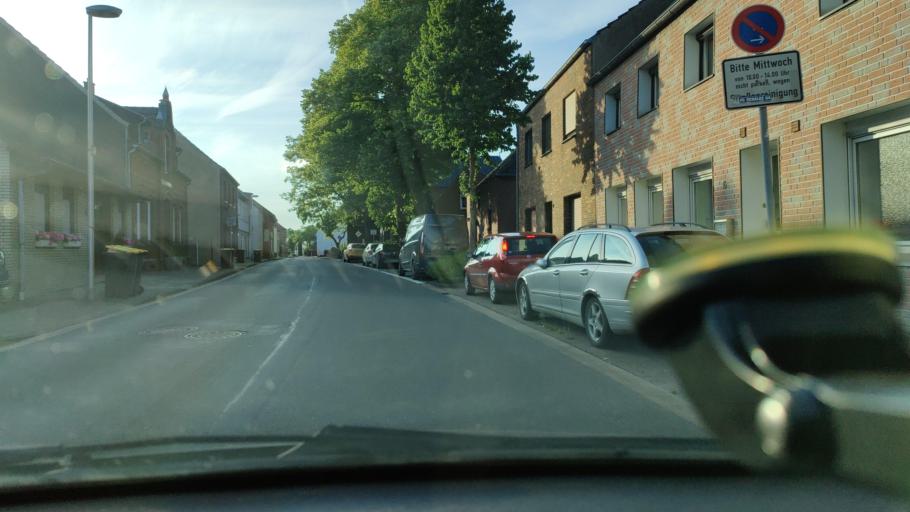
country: DE
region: North Rhine-Westphalia
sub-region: Regierungsbezirk Dusseldorf
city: Rheurdt
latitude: 51.5091
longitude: 6.4714
